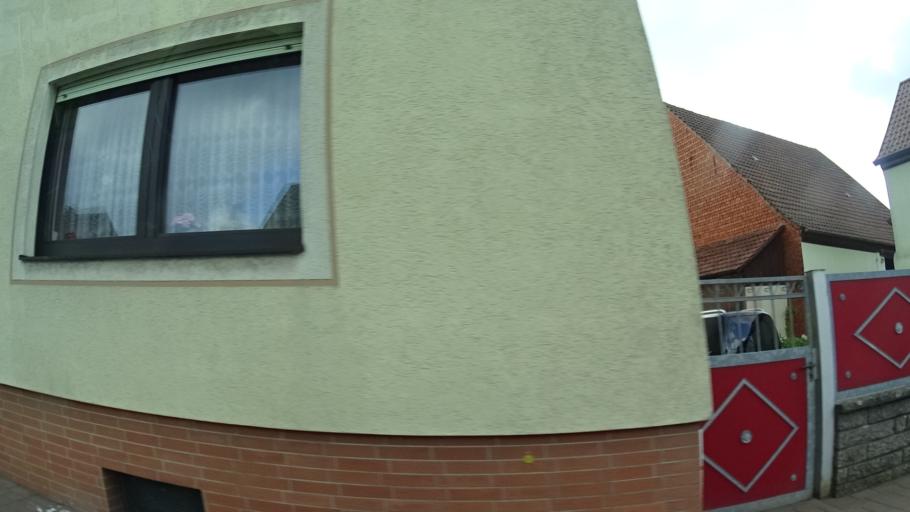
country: DE
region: Bavaria
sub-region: Regierungsbezirk Unterfranken
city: Oberthulba
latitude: 50.2005
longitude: 9.9618
